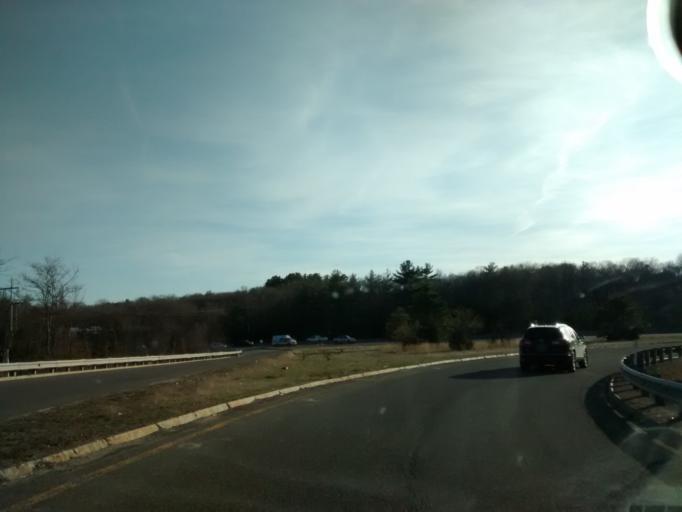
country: US
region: Massachusetts
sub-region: Norfolk County
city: Avon
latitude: 42.1237
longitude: -71.0604
